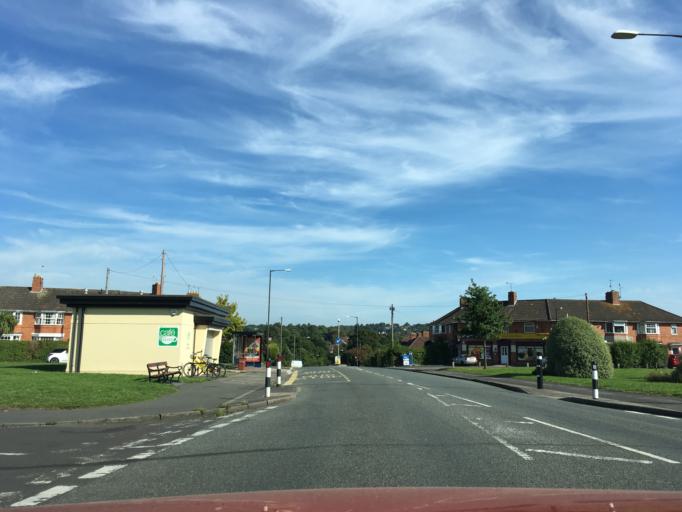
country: GB
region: England
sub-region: North Somerset
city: Easton-in-Gordano
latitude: 51.4881
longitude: -2.6482
